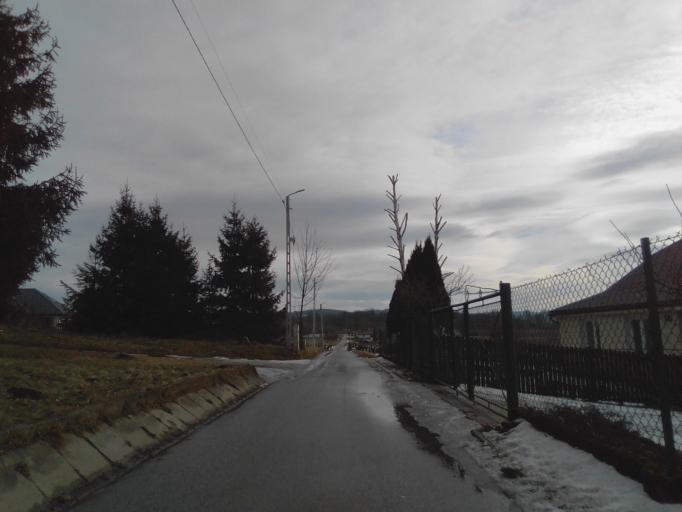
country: PL
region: Subcarpathian Voivodeship
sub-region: Powiat przemyski
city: Dubiecko
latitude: 49.8191
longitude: 22.4072
